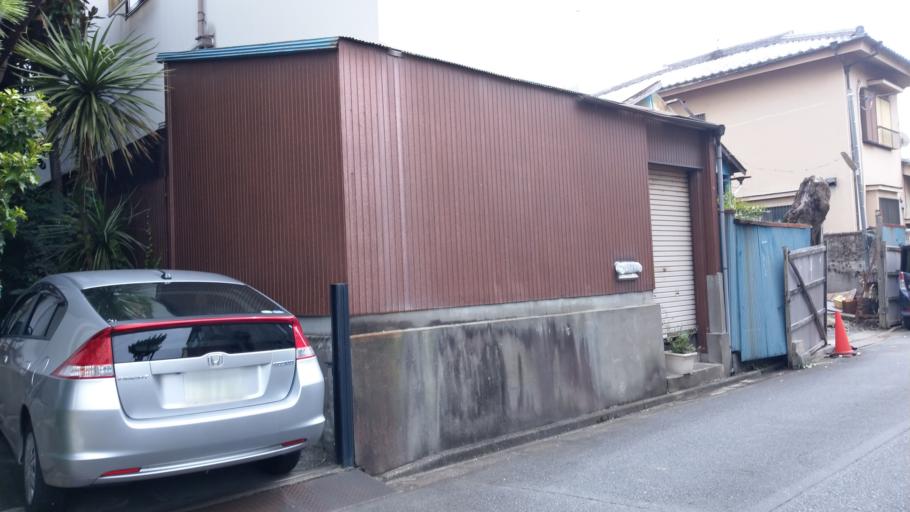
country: JP
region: Saitama
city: Gyoda
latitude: 36.1386
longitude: 139.4597
